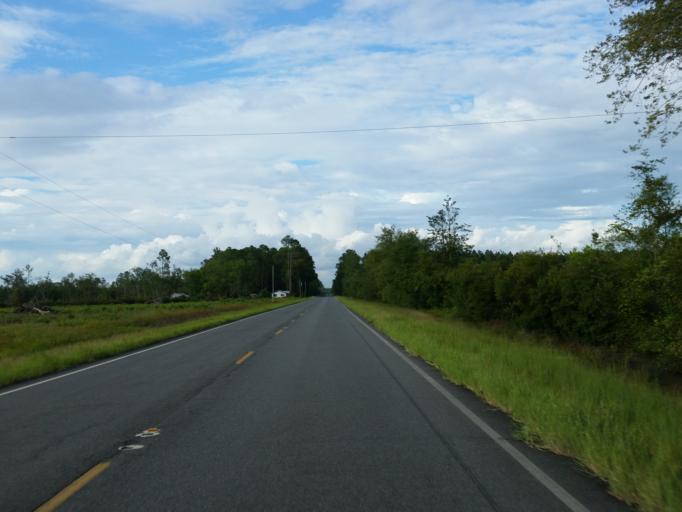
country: US
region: Florida
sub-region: Hamilton County
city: Jasper
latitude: 30.6431
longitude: -82.5762
